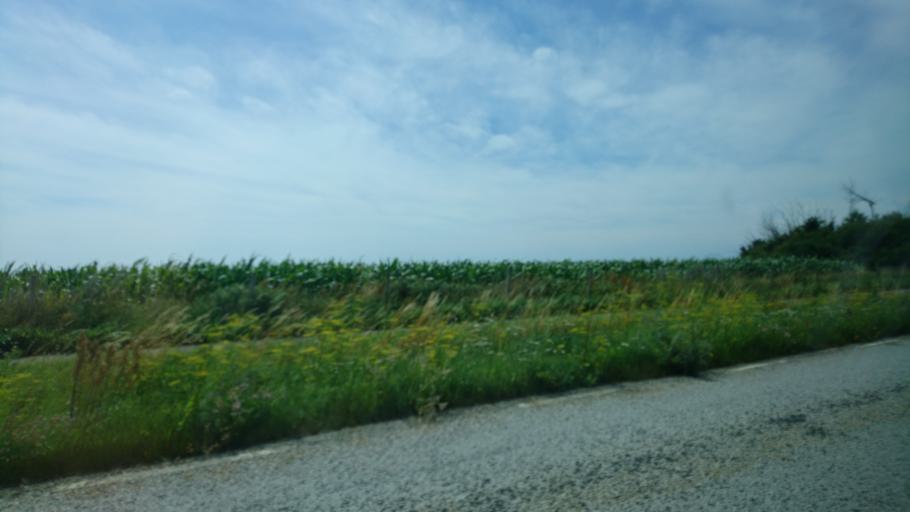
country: SE
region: Skane
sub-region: Skurups Kommun
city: Skivarp
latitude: 55.3872
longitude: 13.5205
